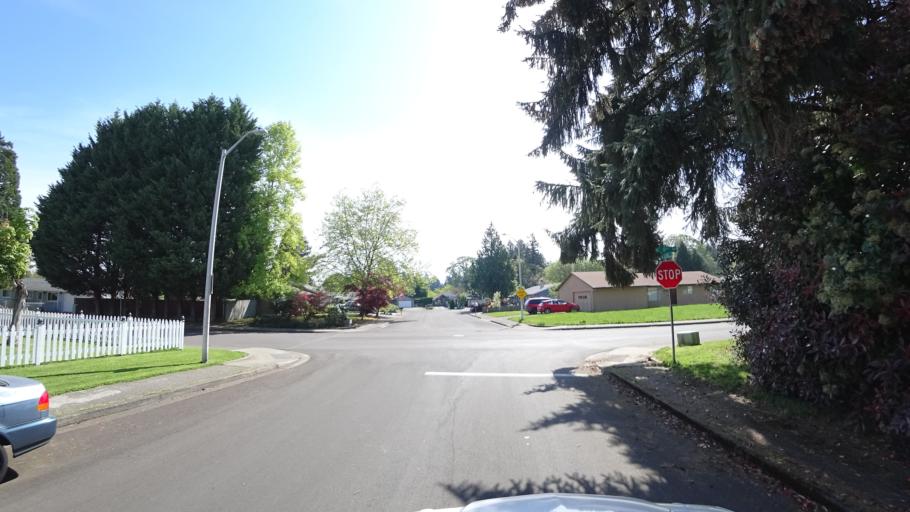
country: US
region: Oregon
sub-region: Washington County
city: Hillsboro
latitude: 45.5261
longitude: -122.9444
